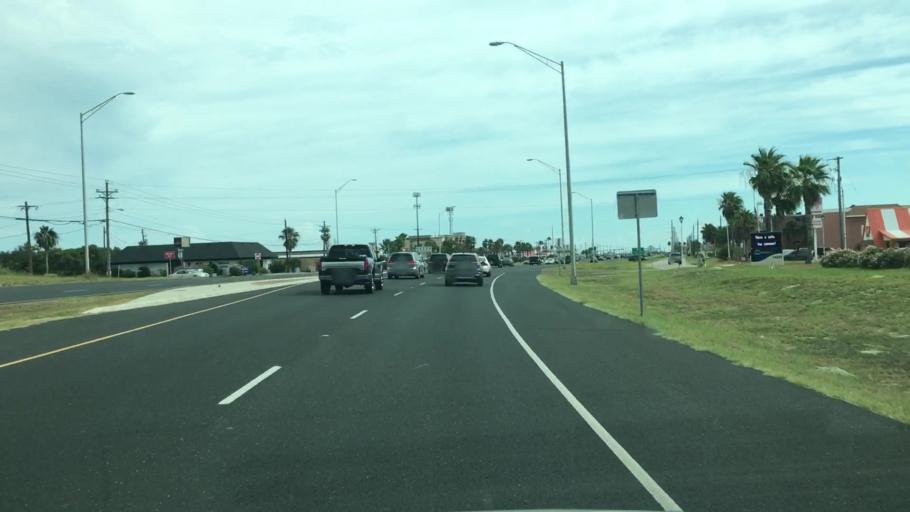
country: US
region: Texas
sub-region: Nueces County
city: Corpus Christi
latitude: 27.6245
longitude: -97.2219
